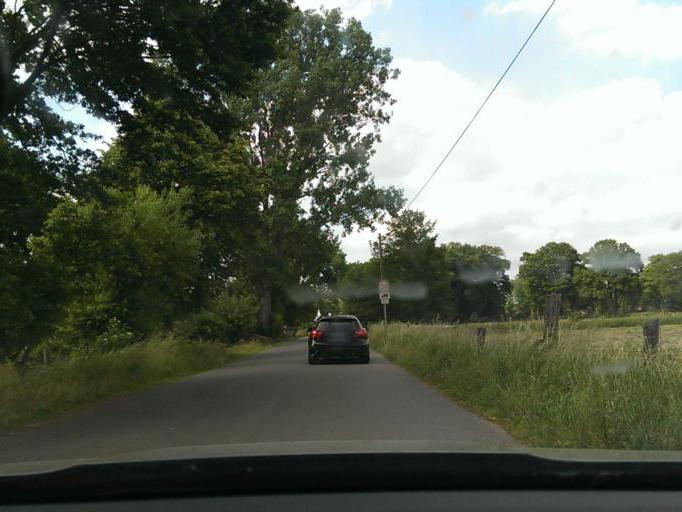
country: DE
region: Lower Saxony
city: Elze
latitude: 52.5186
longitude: 9.7624
